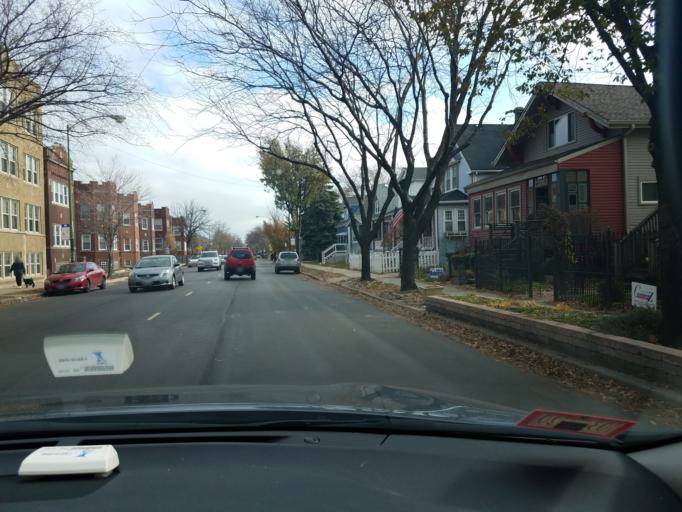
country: US
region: Illinois
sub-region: Cook County
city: Lincolnwood
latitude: 41.9463
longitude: -87.7305
